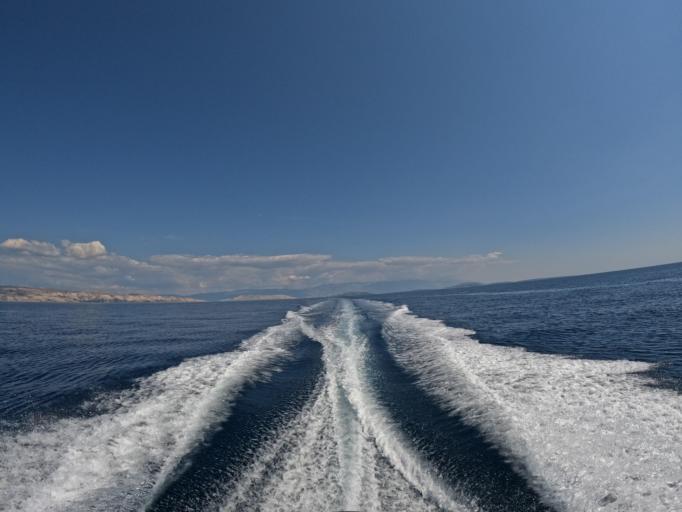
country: HR
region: Primorsko-Goranska
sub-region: Grad Krk
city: Krk
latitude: 44.9220
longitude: 14.5573
